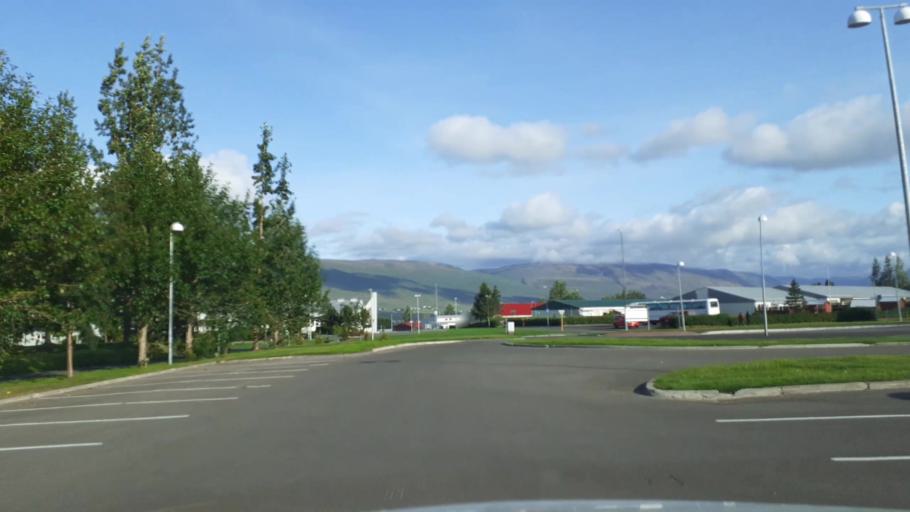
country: IS
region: Northeast
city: Akureyri
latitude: 65.6928
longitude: -18.1362
